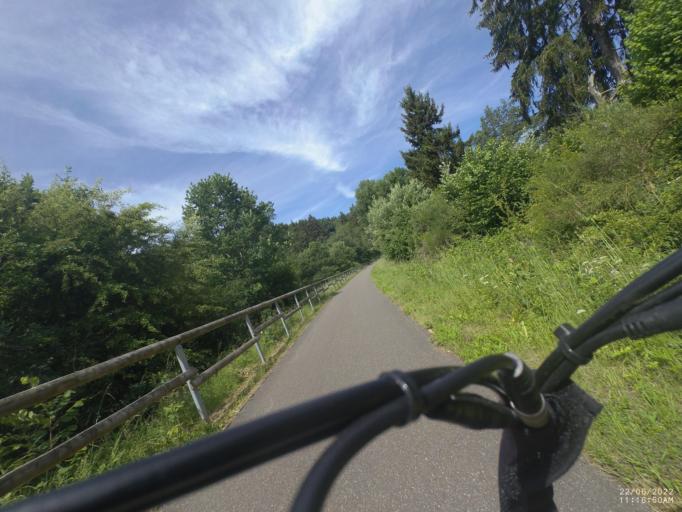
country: DE
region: Rheinland-Pfalz
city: Stadtkyll
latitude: 50.3550
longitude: 6.5187
